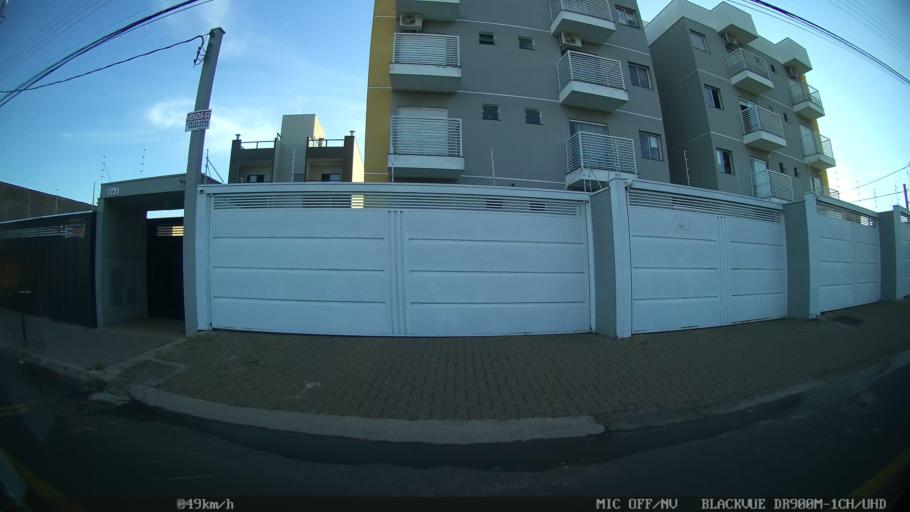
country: BR
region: Sao Paulo
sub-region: Franca
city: Franca
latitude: -20.5175
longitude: -47.3954
